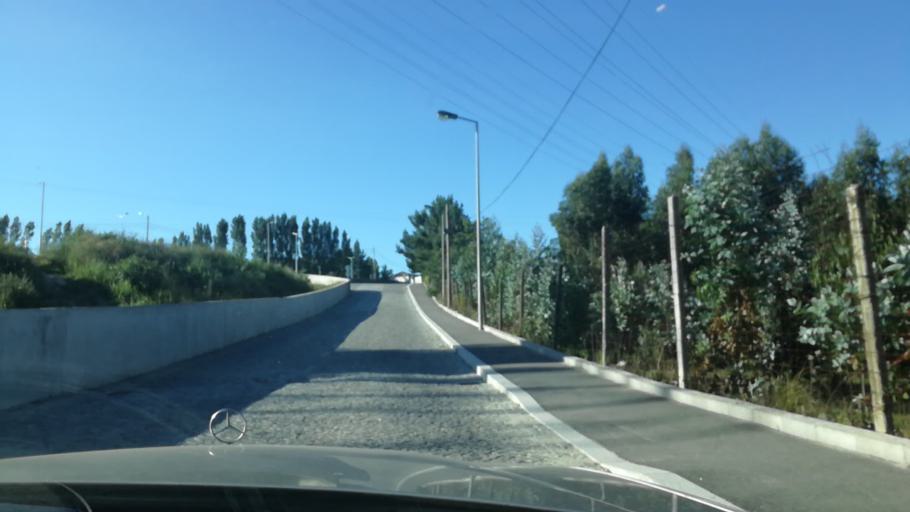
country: PT
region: Porto
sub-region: Maia
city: Leca do Bailio
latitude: 41.2182
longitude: -8.6240
